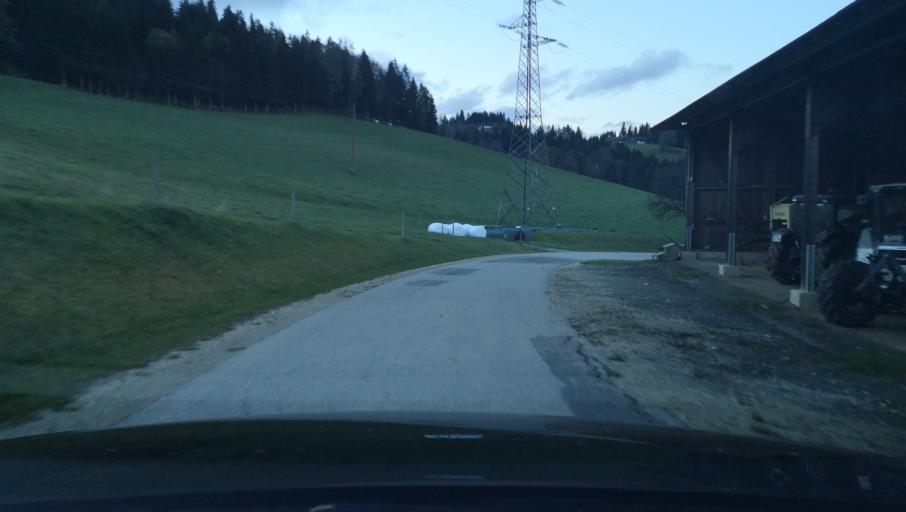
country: AT
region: Styria
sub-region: Politischer Bezirk Weiz
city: Koglhof
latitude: 47.3293
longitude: 15.6838
